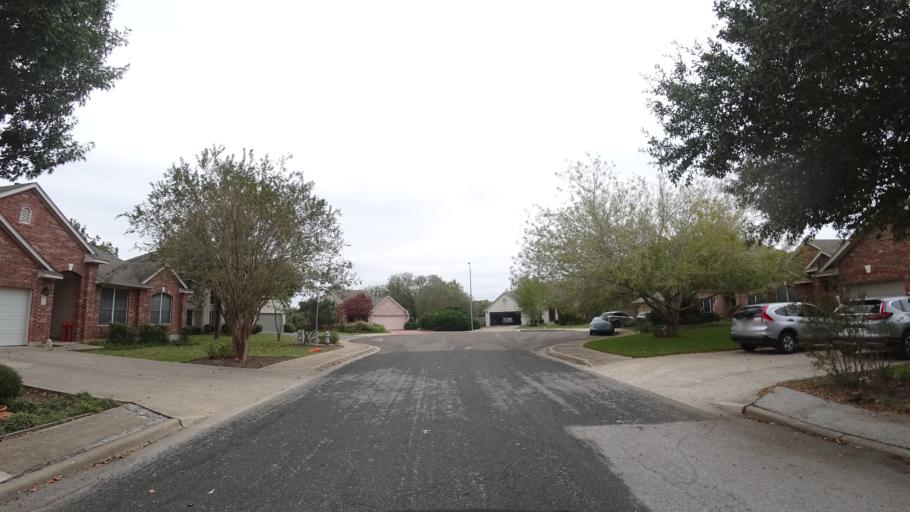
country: US
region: Texas
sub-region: Travis County
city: Shady Hollow
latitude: 30.1547
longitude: -97.8551
